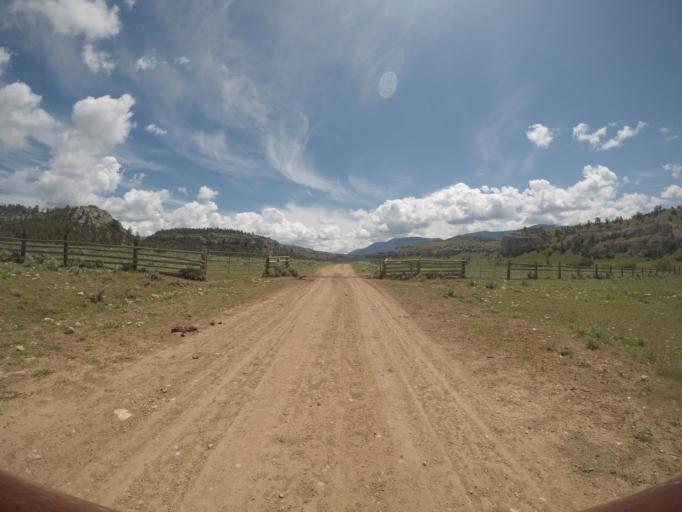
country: US
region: Montana
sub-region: Yellowstone County
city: Laurel
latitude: 45.2412
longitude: -108.6378
